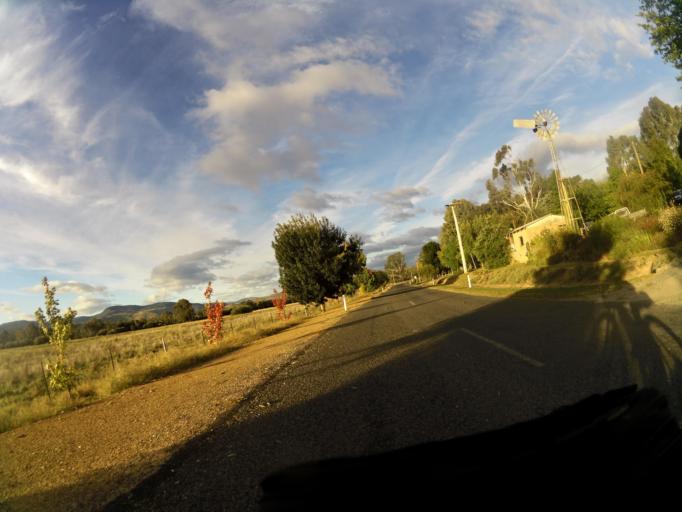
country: AU
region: New South Wales
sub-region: Greater Hume Shire
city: Holbrook
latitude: -36.0470
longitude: 147.9264
